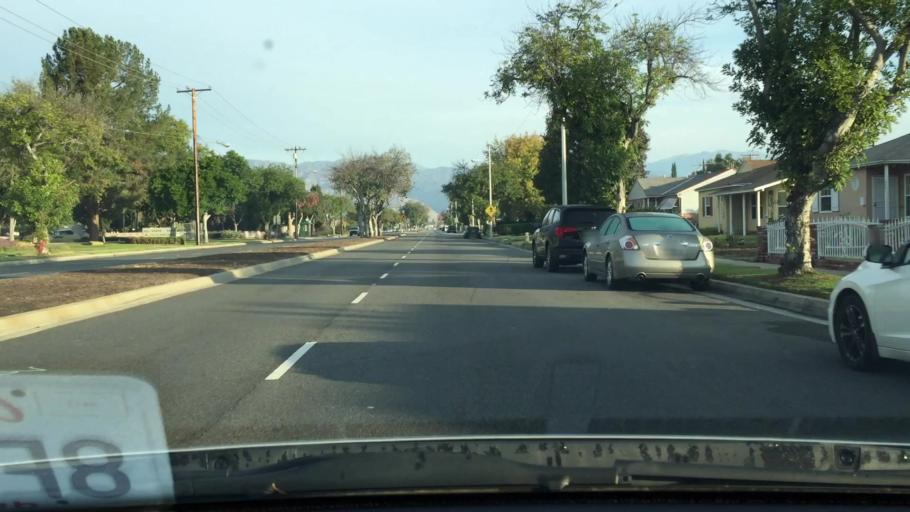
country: US
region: California
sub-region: Los Angeles County
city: West Covina
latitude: 34.0776
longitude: -117.9351
